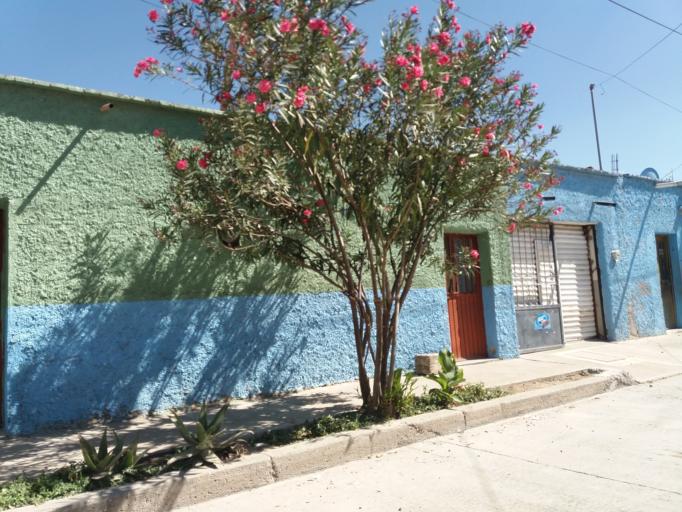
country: MX
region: Aguascalientes
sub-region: Aguascalientes
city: San Sebastian [Fraccionamiento]
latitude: 21.7996
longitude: -102.2739
